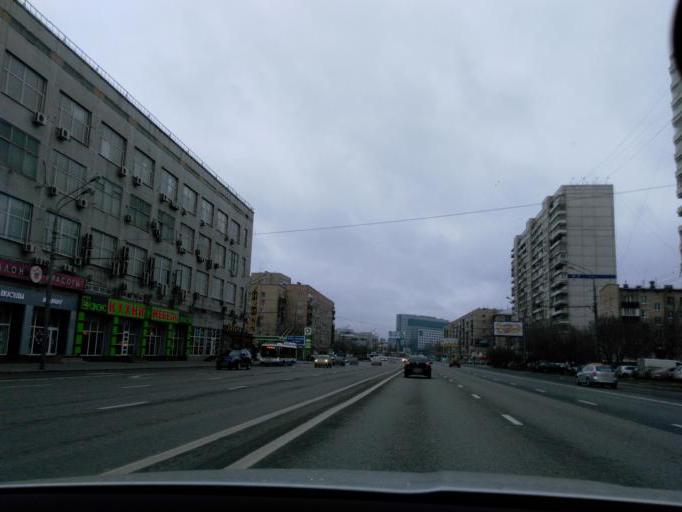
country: RU
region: Moscow
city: Mar'ina Roshcha
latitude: 55.7981
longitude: 37.5839
